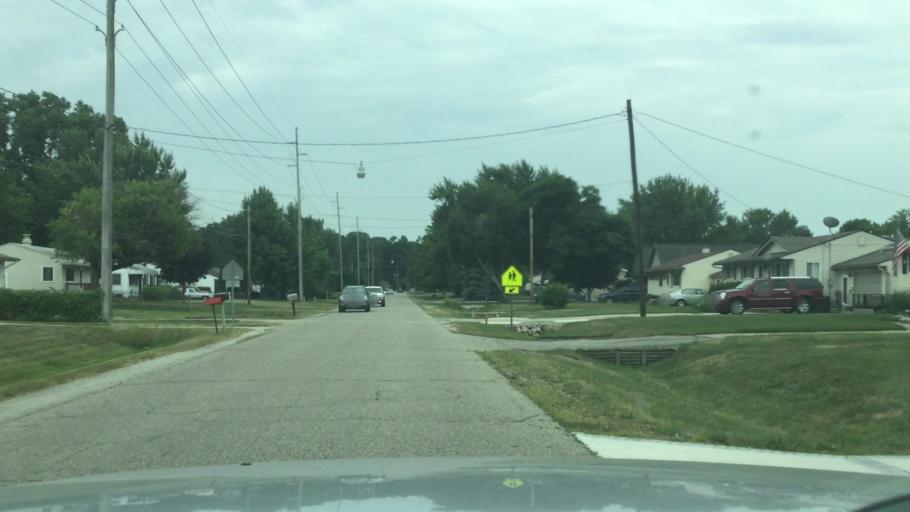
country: US
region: Michigan
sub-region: Genesee County
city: Flint
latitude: 42.9708
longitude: -83.7029
